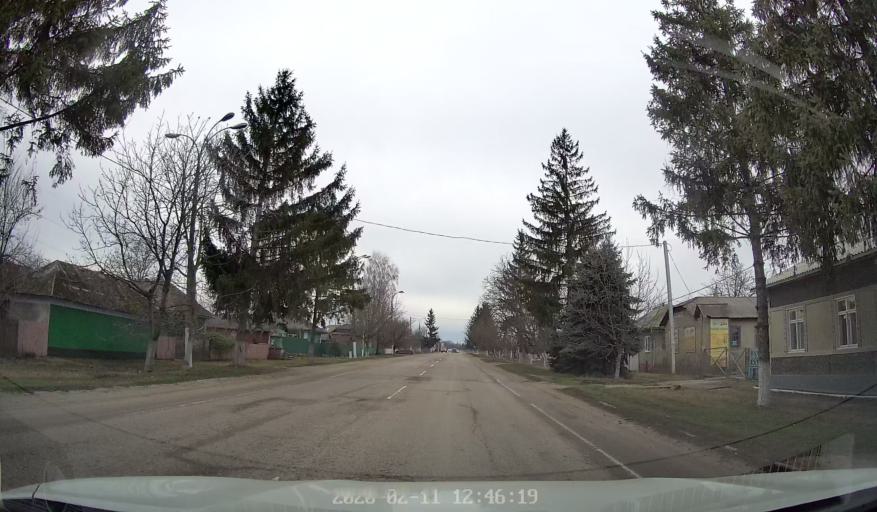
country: MD
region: Briceni
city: Briceni
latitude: 48.2634
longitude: 27.1817
